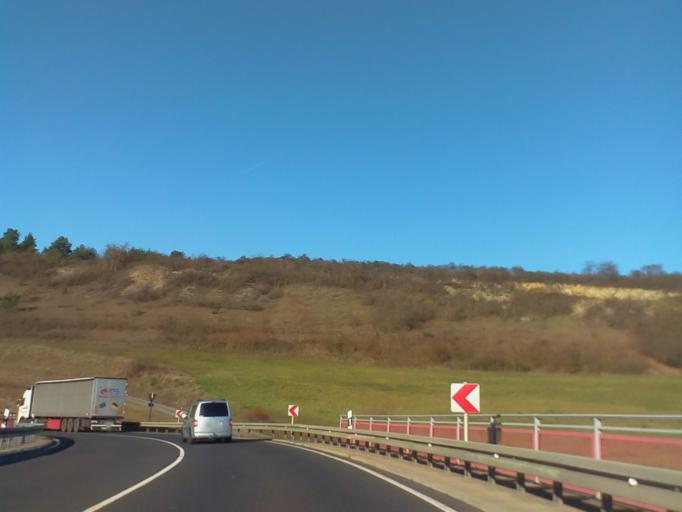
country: DE
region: Bavaria
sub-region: Regierungsbezirk Unterfranken
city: Heustreu
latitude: 50.3403
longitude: 10.2431
